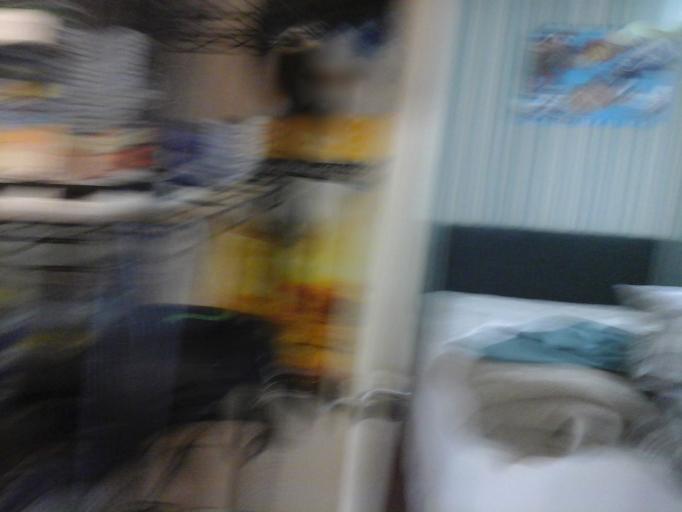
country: GB
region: England
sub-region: Telford and Wrekin
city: Telford
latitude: 52.6589
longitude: -2.4747
